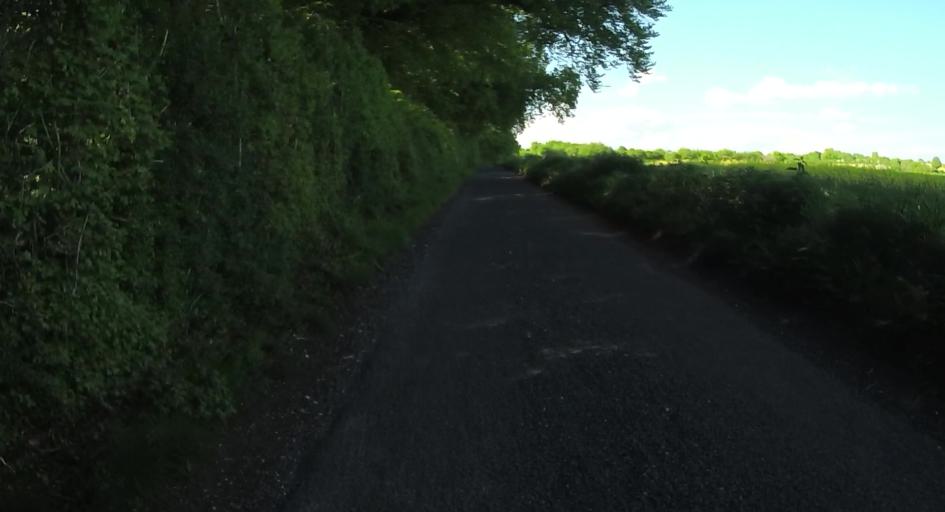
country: GB
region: England
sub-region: Hampshire
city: Overton
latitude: 51.1669
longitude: -1.2197
